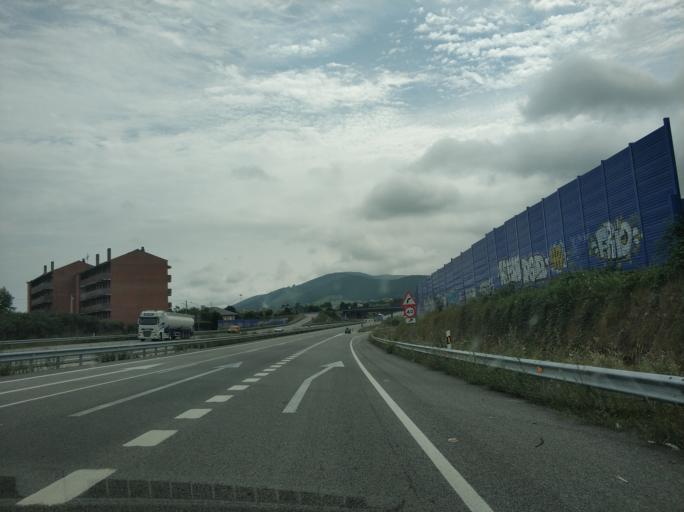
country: ES
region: Asturias
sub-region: Province of Asturias
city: Navia
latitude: 43.5283
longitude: -6.5562
